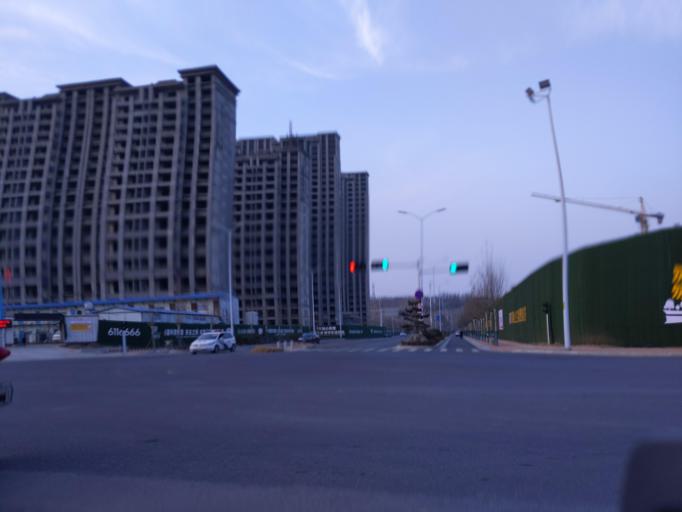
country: CN
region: Henan Sheng
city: Puyang
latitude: 35.8142
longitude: 115.0116
